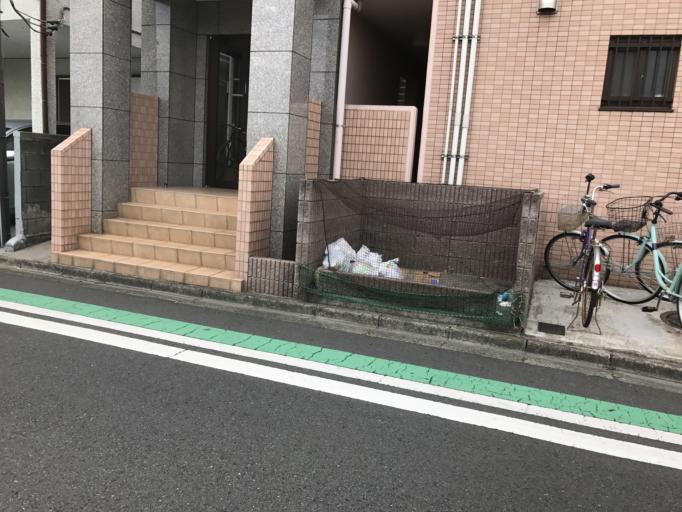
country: JP
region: Tokyo
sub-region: Machida-shi
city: Machida
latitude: 35.5787
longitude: 139.3757
